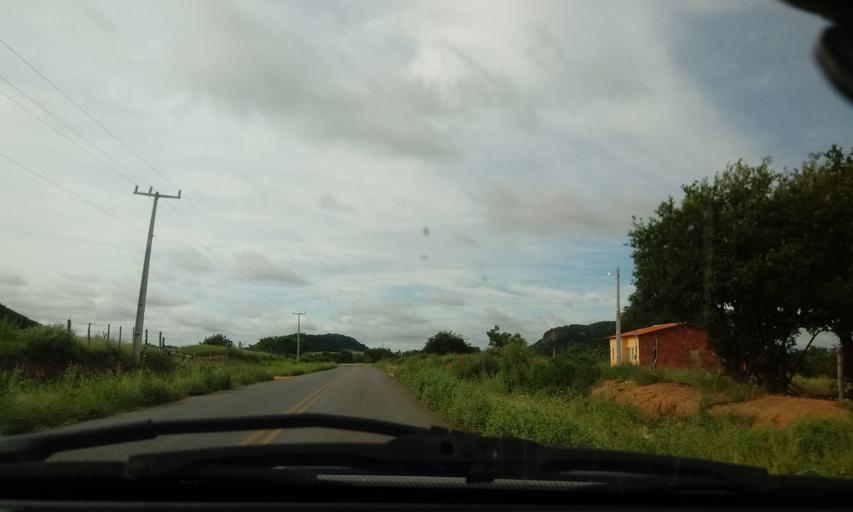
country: BR
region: Bahia
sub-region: Guanambi
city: Guanambi
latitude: -14.1241
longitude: -42.8536
